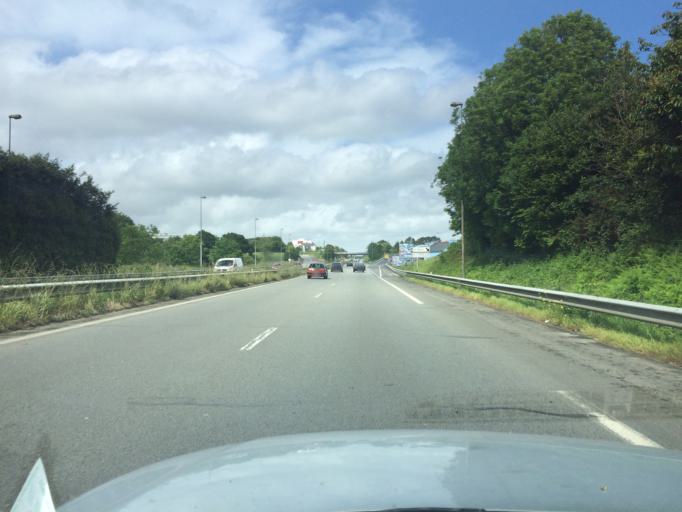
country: FR
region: Brittany
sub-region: Departement du Finistere
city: Brest
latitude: 48.4193
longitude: -4.4781
